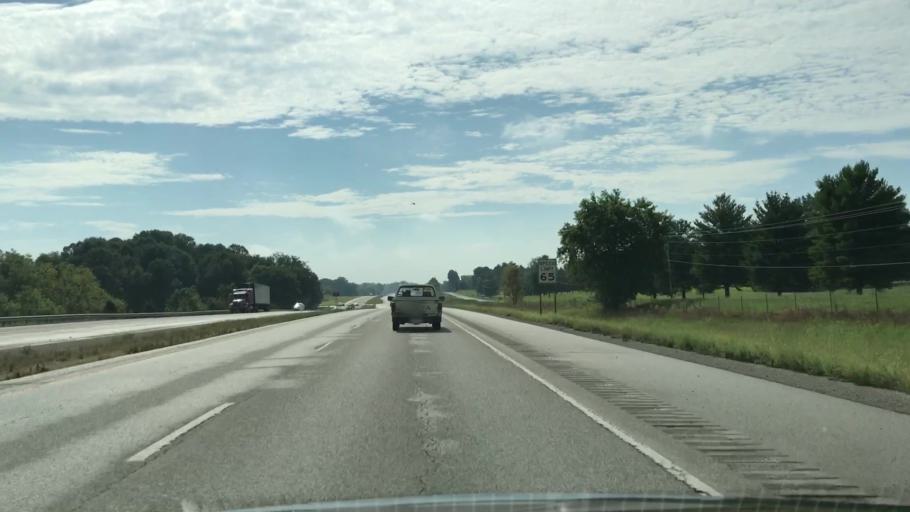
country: US
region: Kentucky
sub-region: Warren County
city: Plano
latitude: 36.8901
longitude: -86.3728
